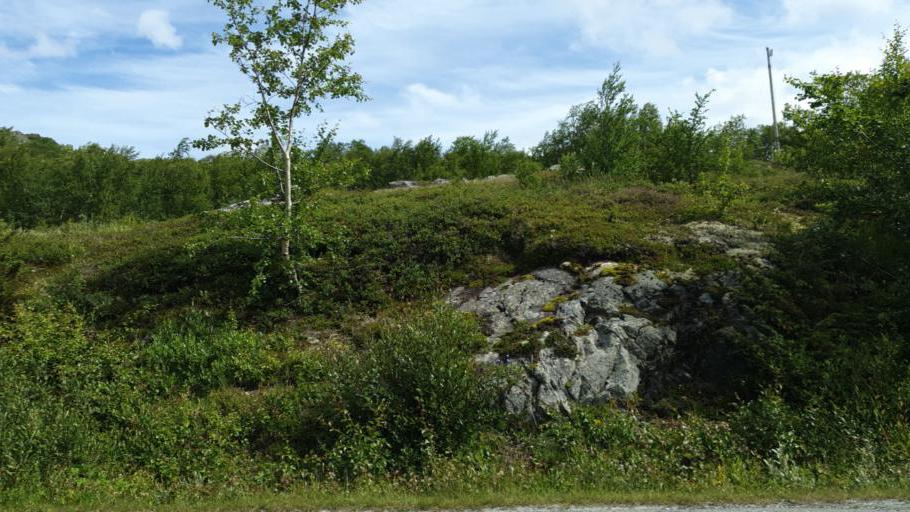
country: NO
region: Oppland
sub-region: Lom
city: Fossbergom
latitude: 61.4929
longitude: 8.8158
